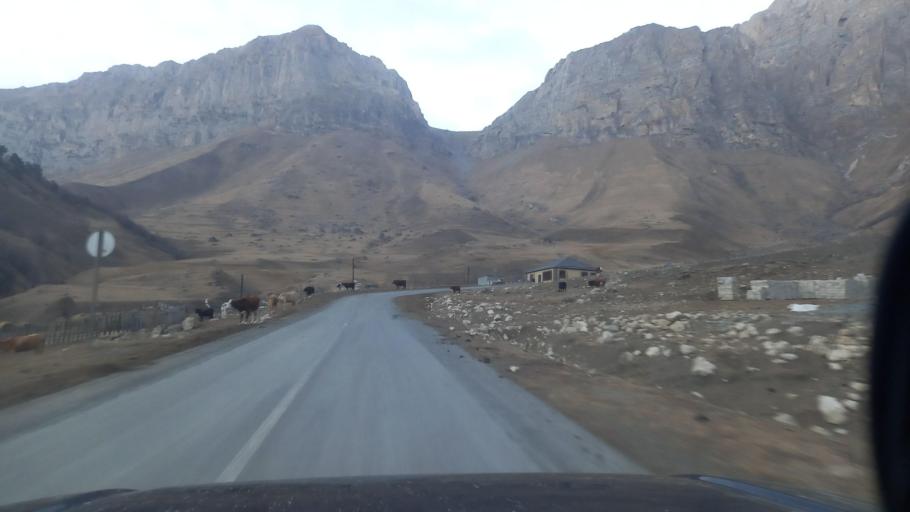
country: RU
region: Ingushetiya
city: Dzhayrakh
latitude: 42.8199
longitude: 44.8159
